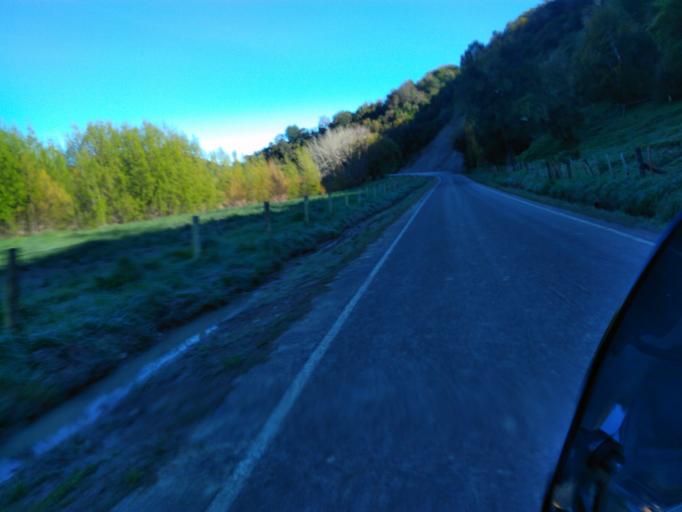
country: NZ
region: Gisborne
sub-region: Gisborne District
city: Gisborne
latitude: -38.4530
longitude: 177.7688
